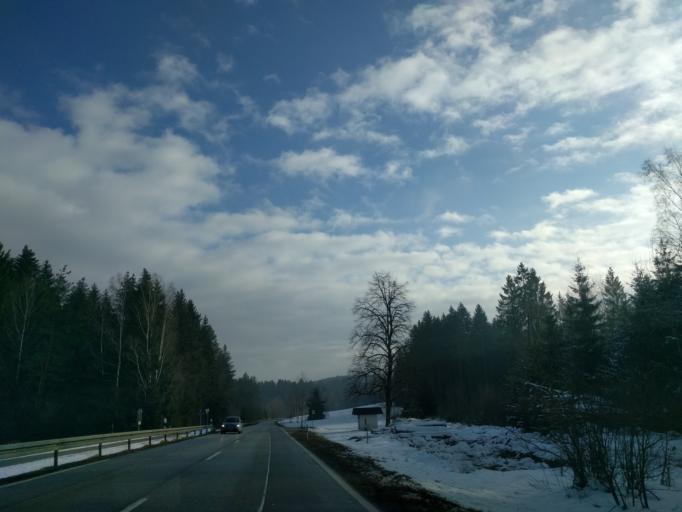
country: DE
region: Bavaria
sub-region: Lower Bavaria
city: Rinchnach
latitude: 48.9891
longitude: 13.1861
